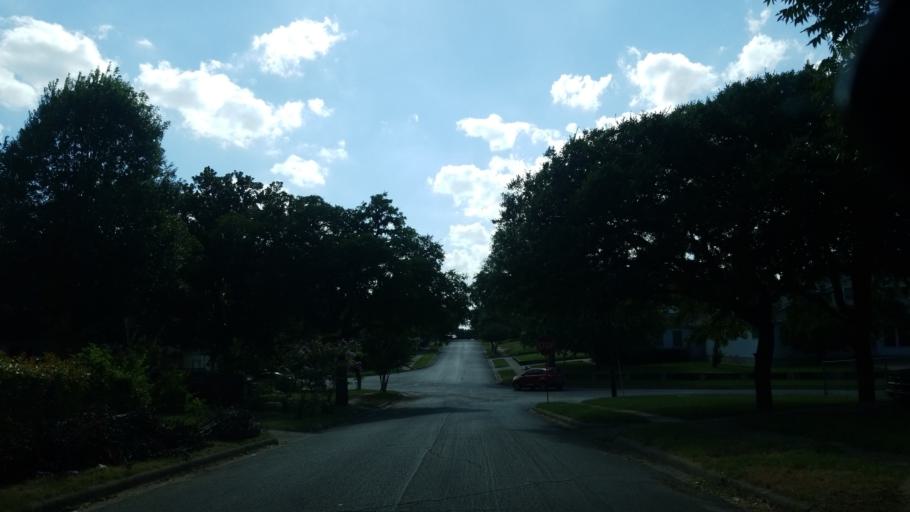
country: US
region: Texas
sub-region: Dallas County
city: Balch Springs
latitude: 32.7672
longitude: -96.7049
